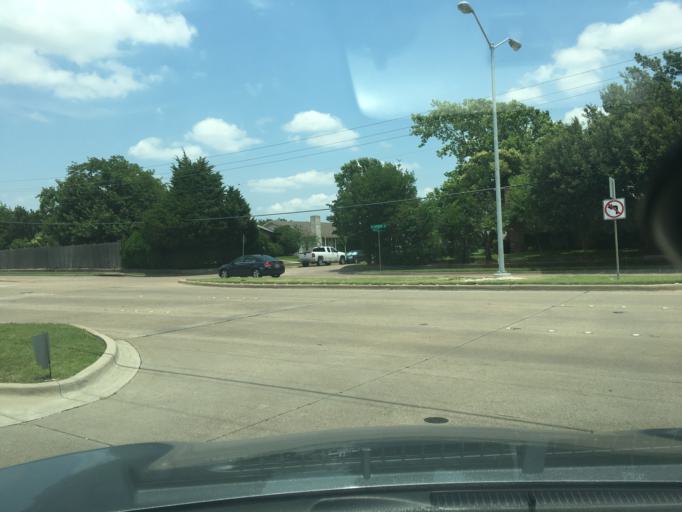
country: US
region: Texas
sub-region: Dallas County
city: Richardson
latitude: 32.9548
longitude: -96.6829
